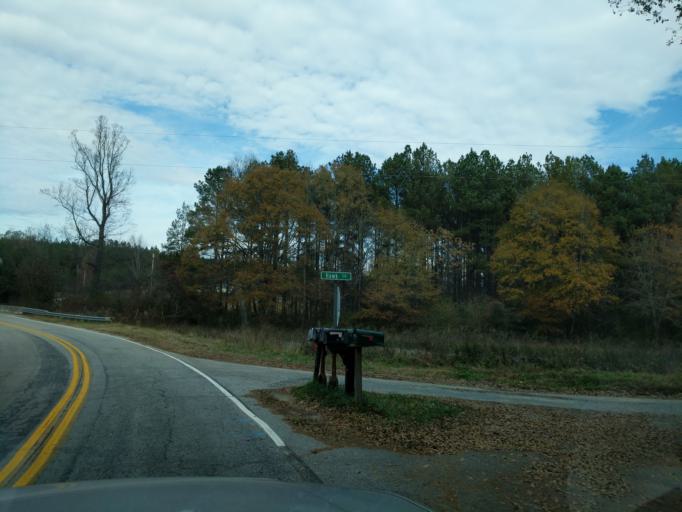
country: US
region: South Carolina
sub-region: Pickens County
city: Arial
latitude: 34.8855
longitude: -82.6447
